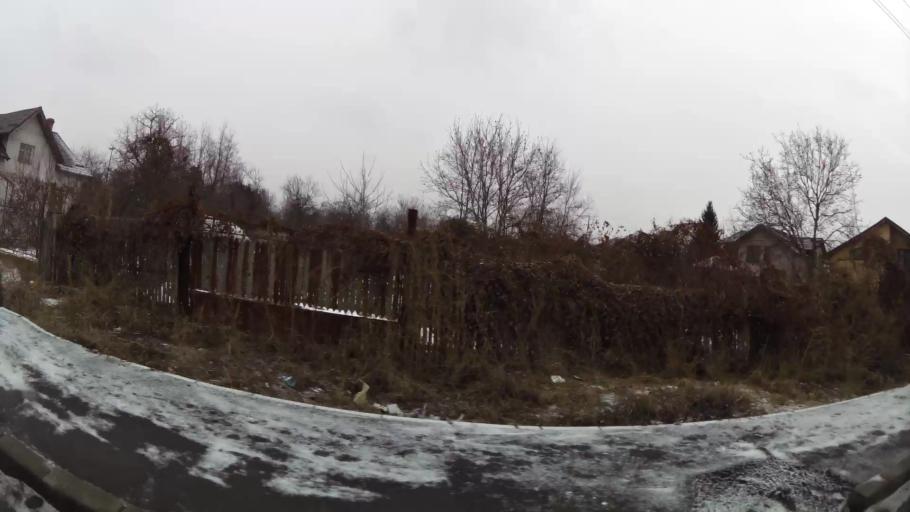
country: RO
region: Dambovita
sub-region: Municipiul Targoviste
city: Targoviste
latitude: 44.9379
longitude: 25.4678
